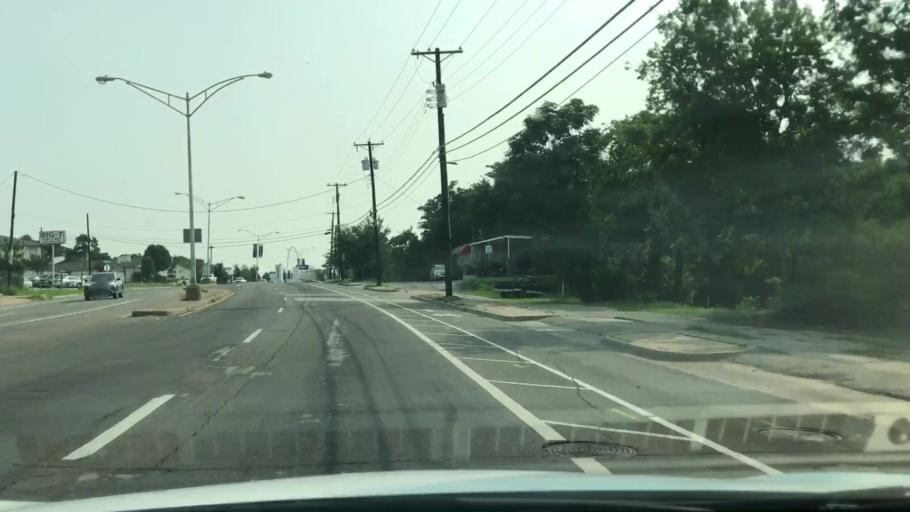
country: US
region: Texas
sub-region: Dallas County
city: Dallas
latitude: 32.7672
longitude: -96.8400
